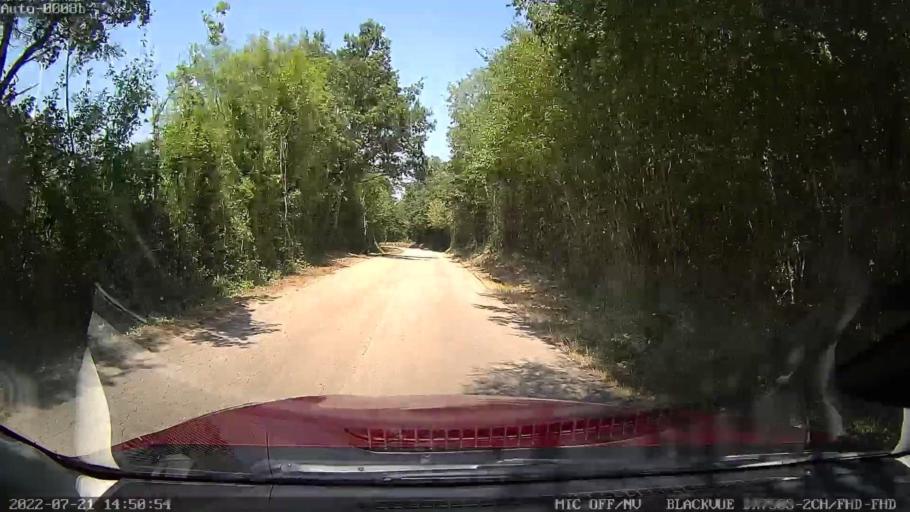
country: HR
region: Istarska
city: Pazin
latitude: 45.1645
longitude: 13.9183
